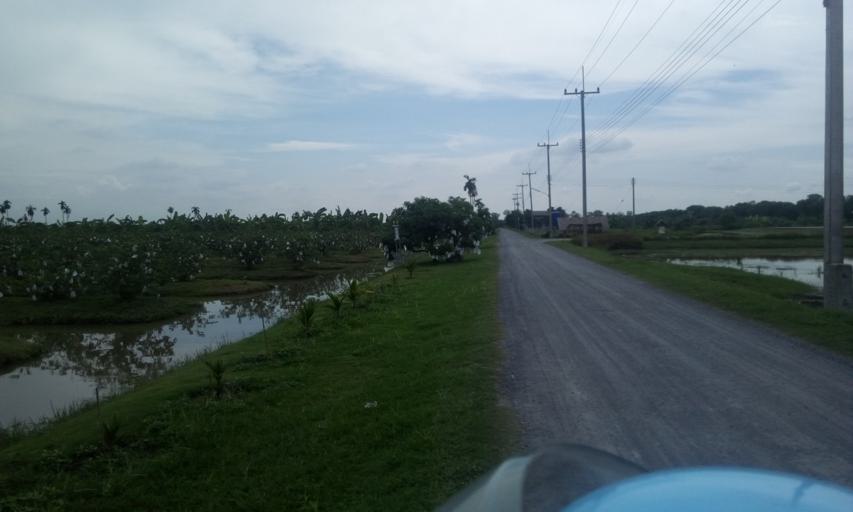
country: TH
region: Pathum Thani
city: Ban Lam Luk Ka
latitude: 13.9897
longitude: 100.8383
